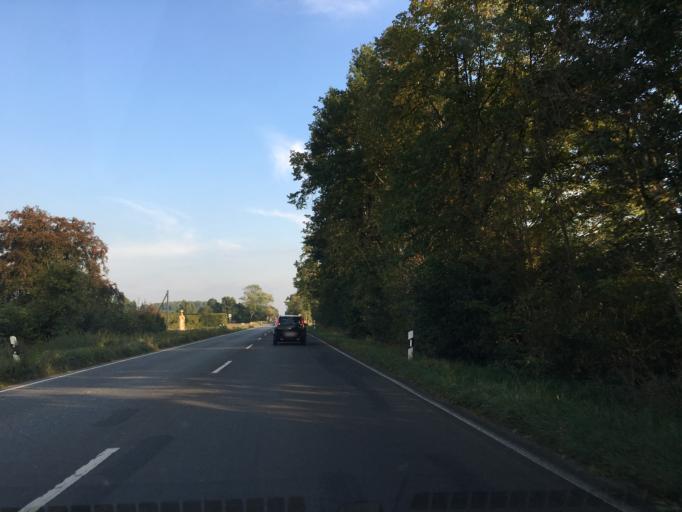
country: DE
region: North Rhine-Westphalia
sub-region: Regierungsbezirk Munster
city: Altenberge
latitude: 52.0179
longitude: 7.5077
